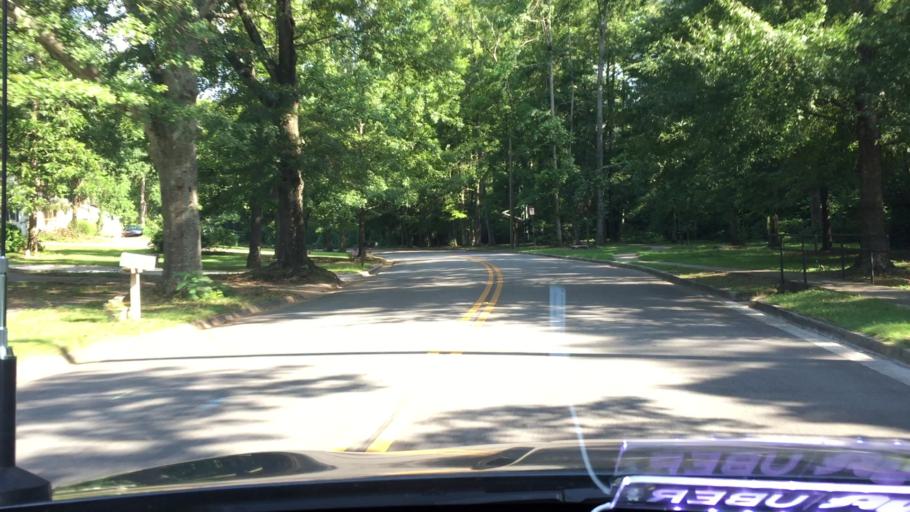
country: US
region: Alabama
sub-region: Lee County
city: Auburn
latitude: 32.6033
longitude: -85.4747
